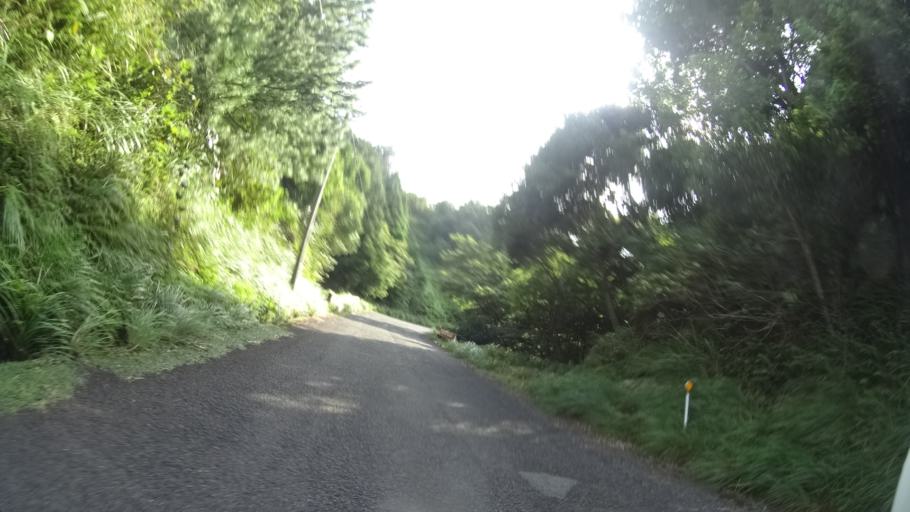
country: JP
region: Kagoshima
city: Nishinoomote
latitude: 30.3864
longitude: 130.3824
